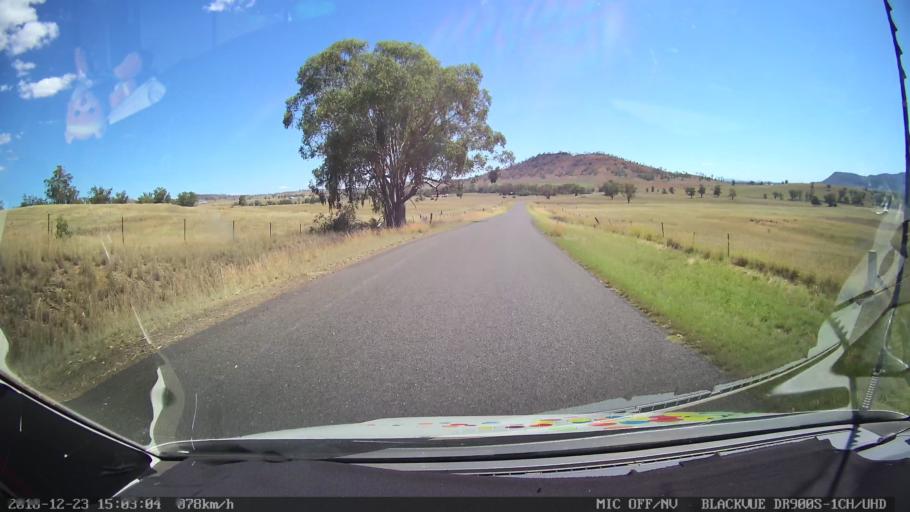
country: AU
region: New South Wales
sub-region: Tamworth Municipality
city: Manilla
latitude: -30.7349
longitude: 150.7688
